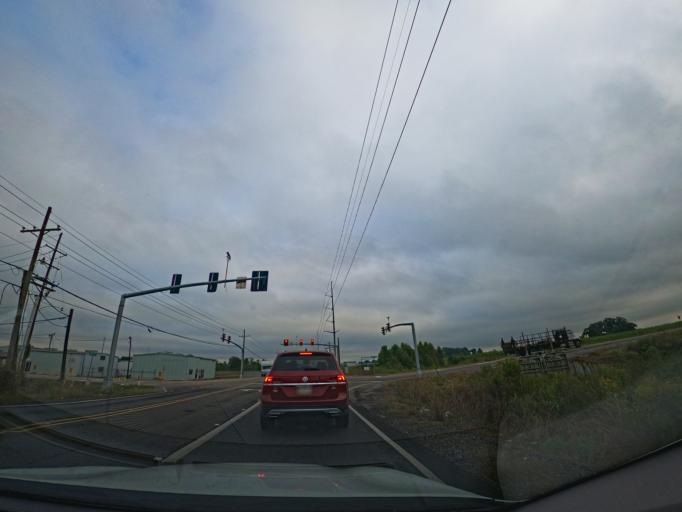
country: US
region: Louisiana
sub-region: Terrebonne Parish
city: Presquille
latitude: 29.5451
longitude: -90.6784
